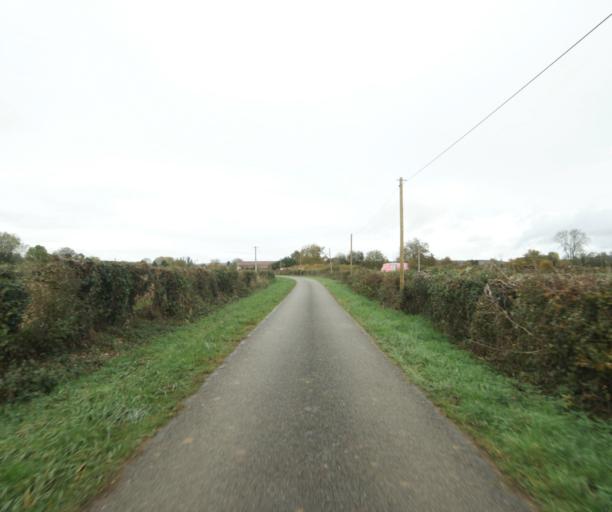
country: FR
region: Rhone-Alpes
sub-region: Departement de l'Ain
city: Pont-de-Vaux
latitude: 46.4712
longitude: 4.9040
